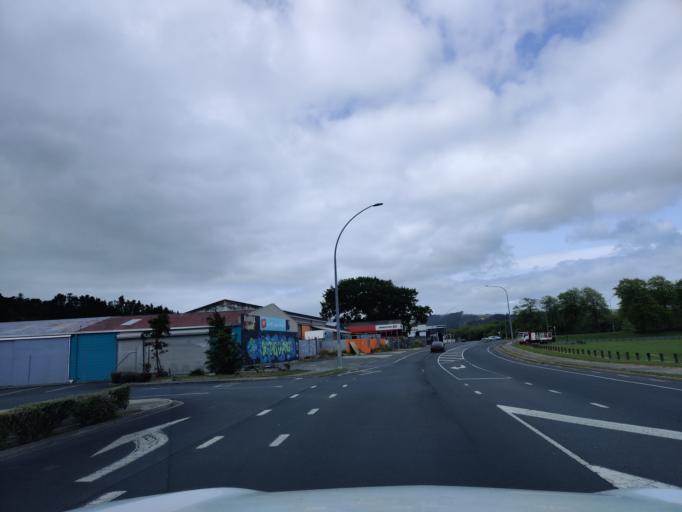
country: NZ
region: Waikato
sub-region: Waikato District
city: Ngaruawahia
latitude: -37.5651
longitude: 175.1583
